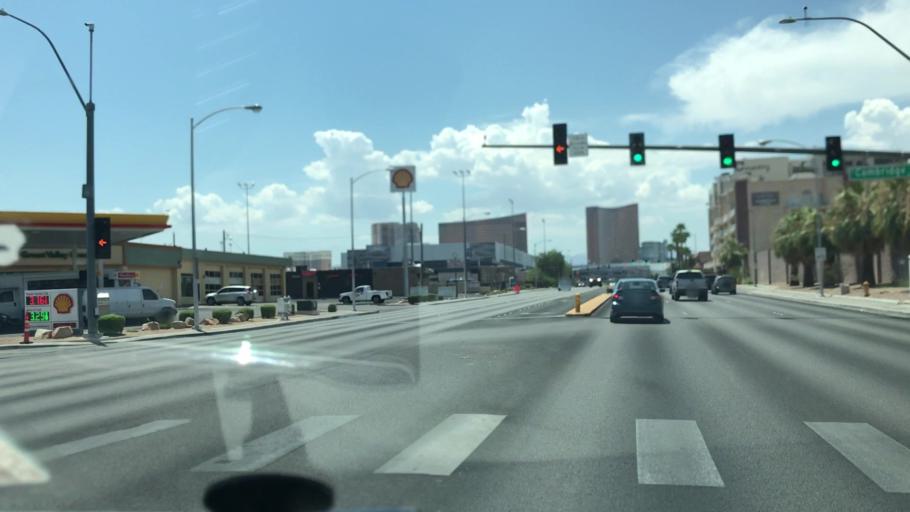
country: US
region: Nevada
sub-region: Clark County
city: Winchester
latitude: 36.1298
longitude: -115.1413
